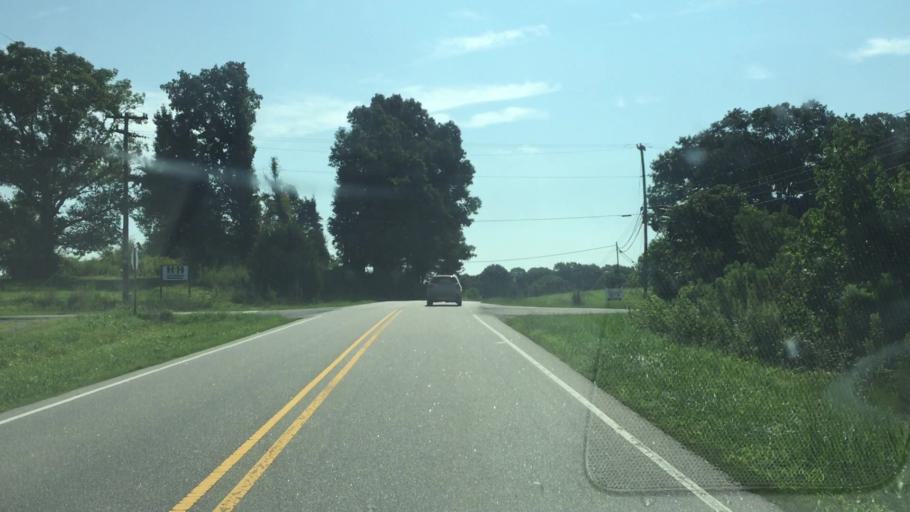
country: US
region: North Carolina
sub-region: Union County
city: Fairview
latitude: 35.1425
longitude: -80.5053
